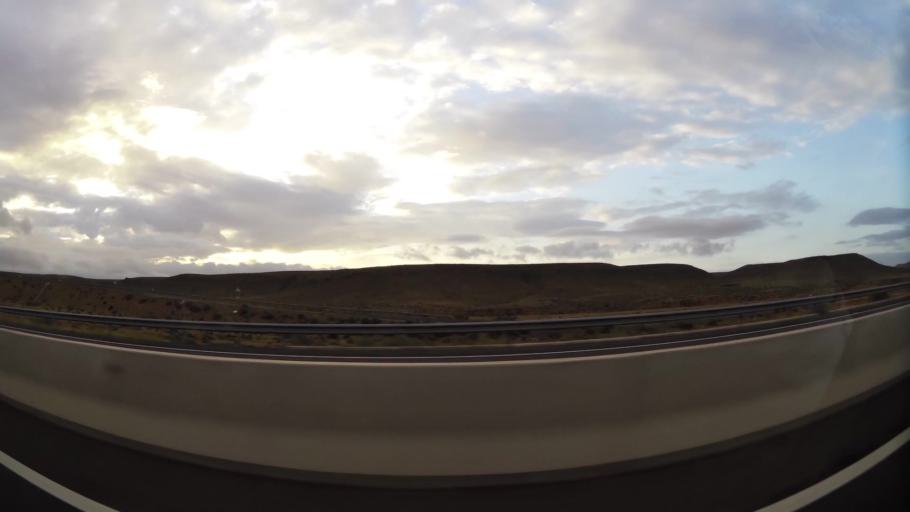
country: MA
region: Oriental
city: Taourirt
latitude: 34.4461
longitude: -3.0579
